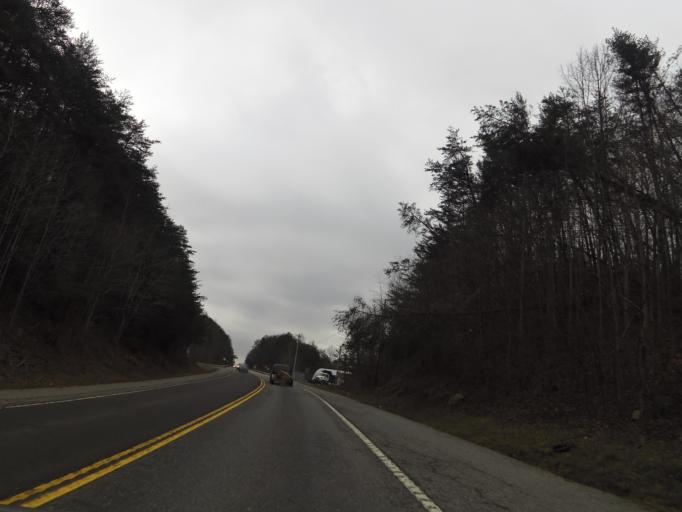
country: US
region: Tennessee
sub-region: Campbell County
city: Jacksboro
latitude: 36.3850
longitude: -84.2563
